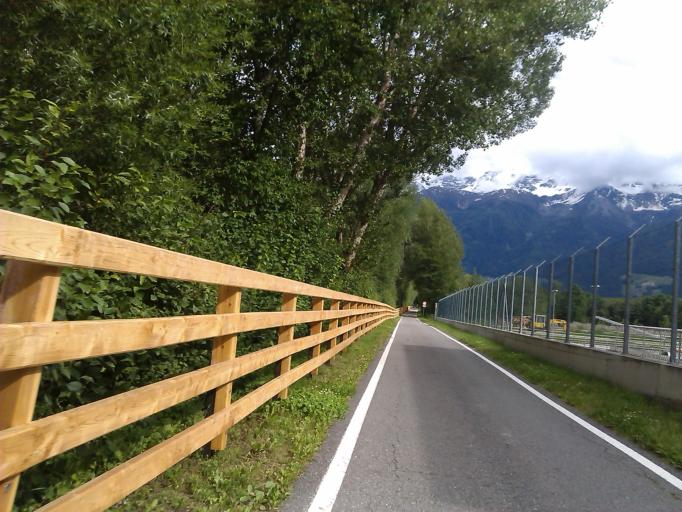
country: IT
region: Trentino-Alto Adige
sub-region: Bolzano
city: Sluderno
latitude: 46.6575
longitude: 10.5680
